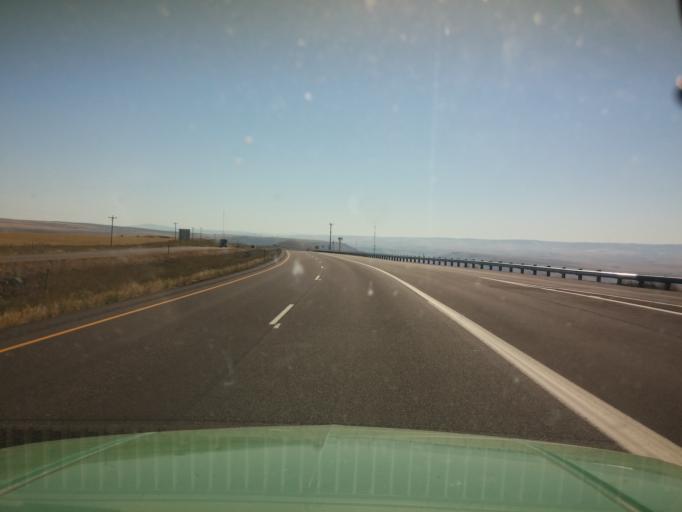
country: US
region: Idaho
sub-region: Nez Perce County
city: Lewiston
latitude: 46.4618
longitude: -117.0150
